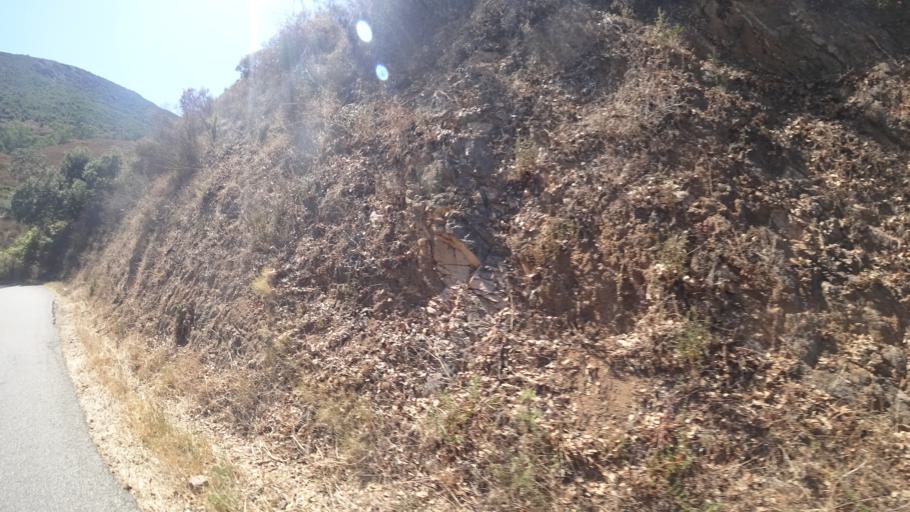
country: FR
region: Corsica
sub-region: Departement de la Corse-du-Sud
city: Alata
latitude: 41.9683
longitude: 8.7084
